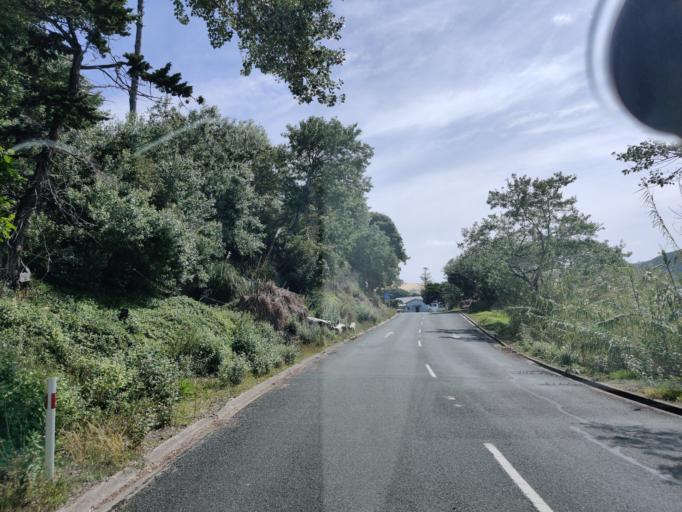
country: NZ
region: Northland
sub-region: Far North District
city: Ahipara
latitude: -35.5038
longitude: 173.3947
